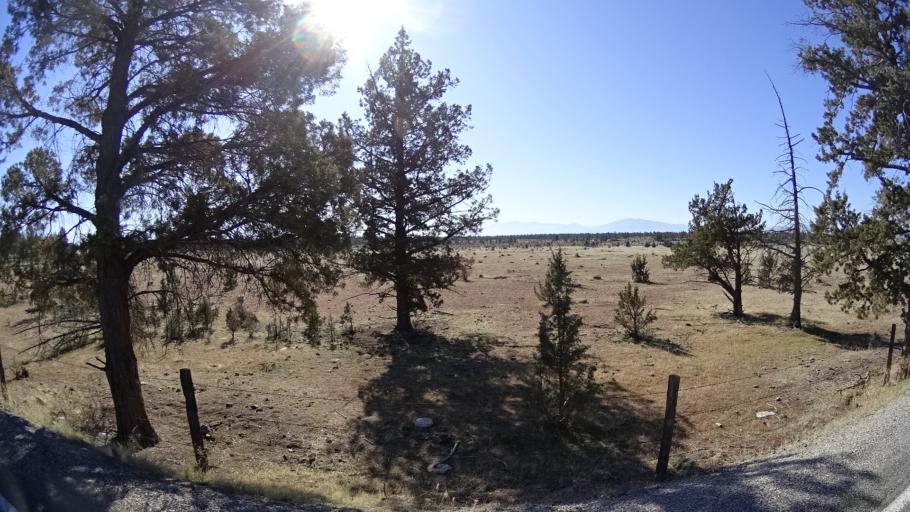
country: US
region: California
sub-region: Siskiyou County
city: Montague
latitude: 41.6596
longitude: -122.4011
